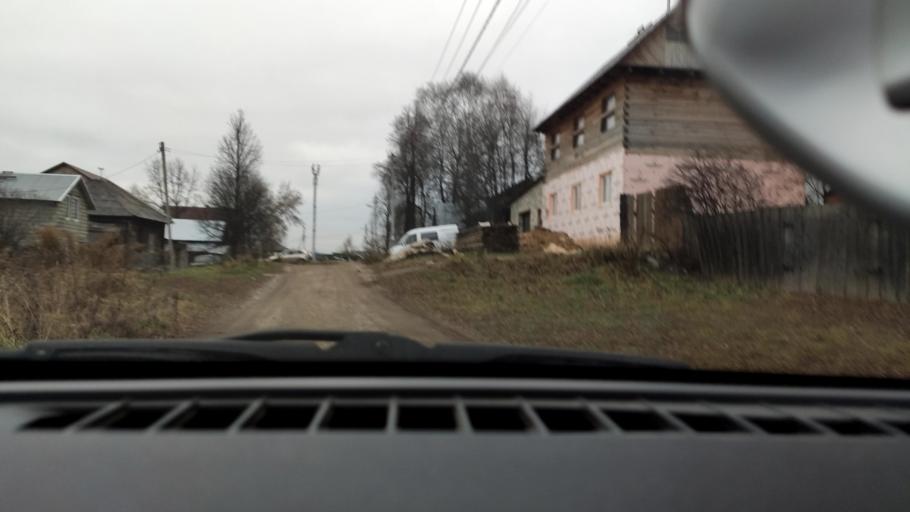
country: RU
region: Perm
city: Perm
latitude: 58.0290
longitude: 56.3349
